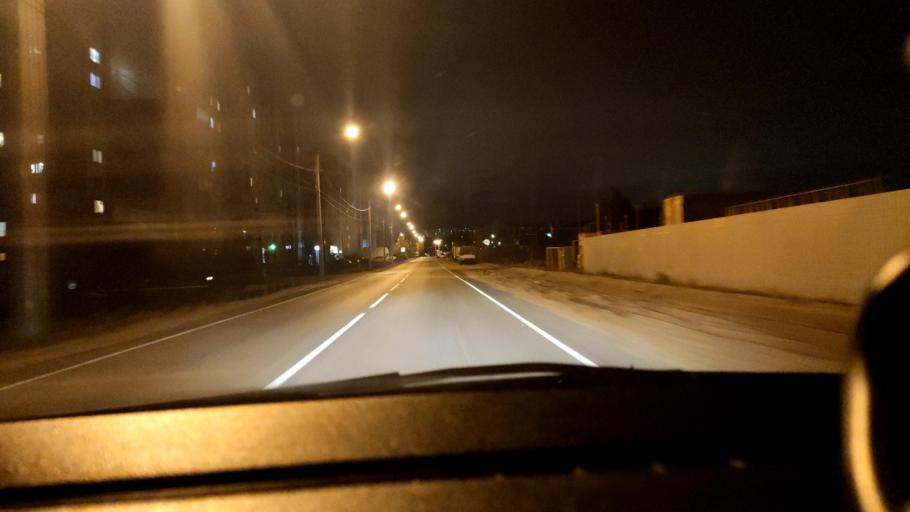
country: RU
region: Voronezj
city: Pridonskoy
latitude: 51.6186
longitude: 39.0628
